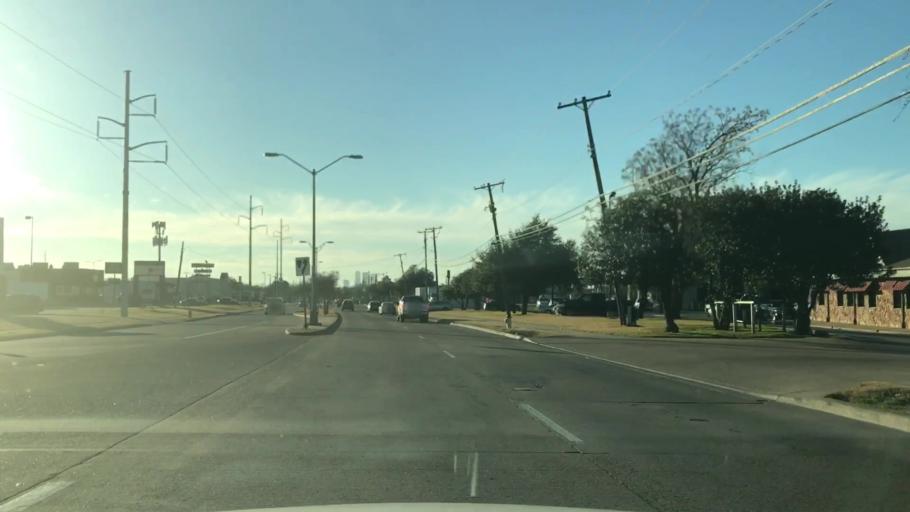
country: US
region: Texas
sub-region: Dallas County
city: Balch Springs
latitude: 32.7926
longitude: -96.6959
